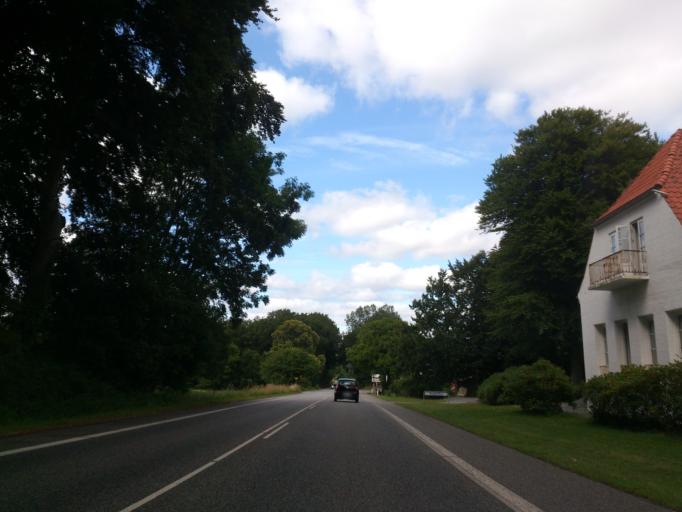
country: DK
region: South Denmark
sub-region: Aabenraa Kommune
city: Krusa
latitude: 54.9352
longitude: 9.4507
